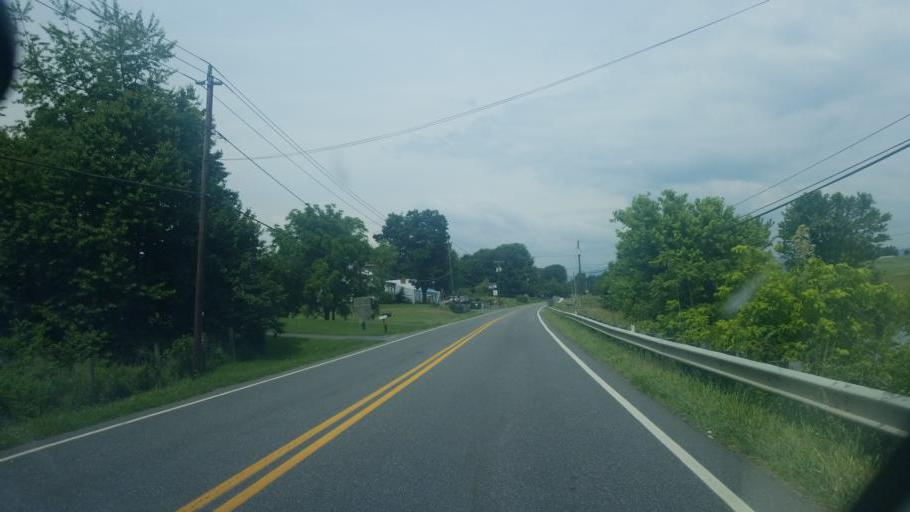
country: US
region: Virginia
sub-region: Rockingham County
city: Dayton
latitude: 38.4577
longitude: -78.9518
